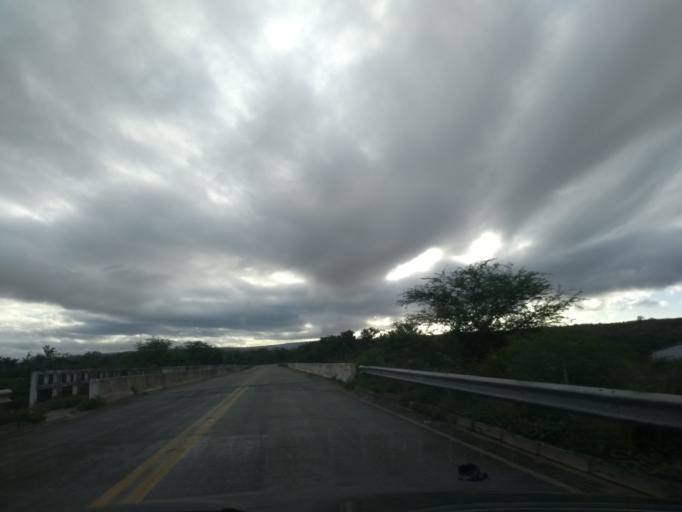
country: BR
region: Bahia
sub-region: Ituacu
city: Ituacu
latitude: -13.7682
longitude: -41.0430
